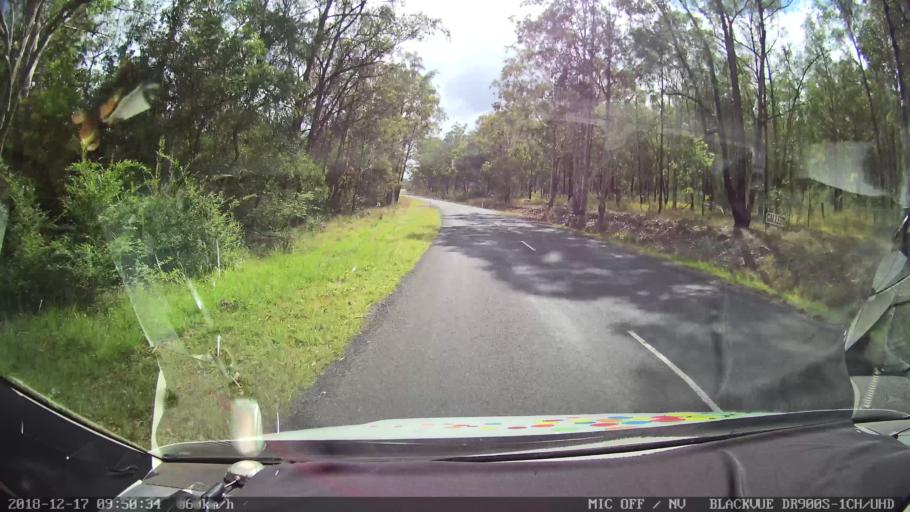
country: AU
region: New South Wales
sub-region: Tenterfield Municipality
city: Carrolls Creek
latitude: -28.9265
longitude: 152.3655
